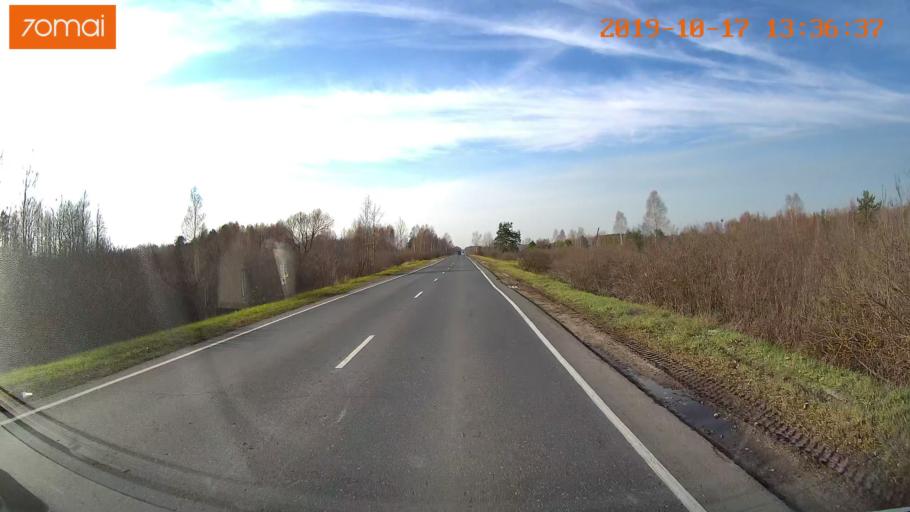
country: RU
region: Rjazan
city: Tuma
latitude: 55.1397
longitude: 40.6596
